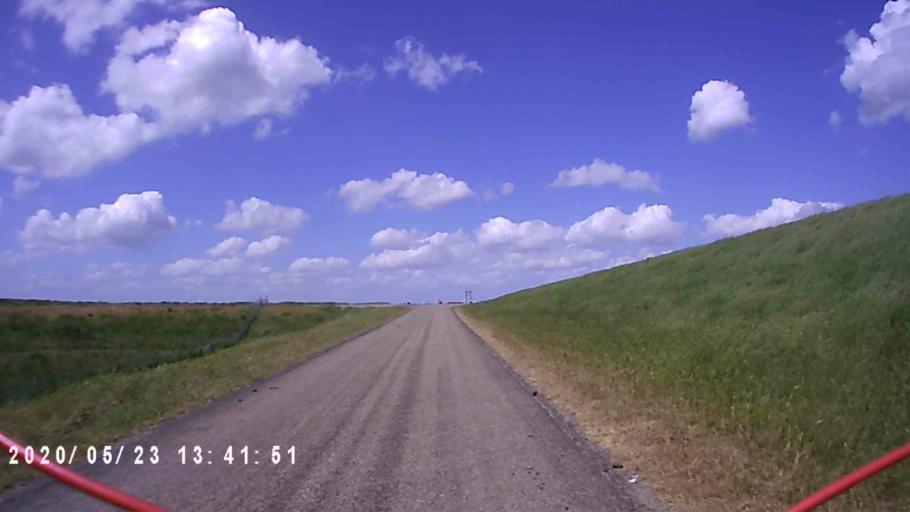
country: NL
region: Groningen
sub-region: Gemeente  Oldambt
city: Winschoten
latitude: 53.2639
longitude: 7.0713
